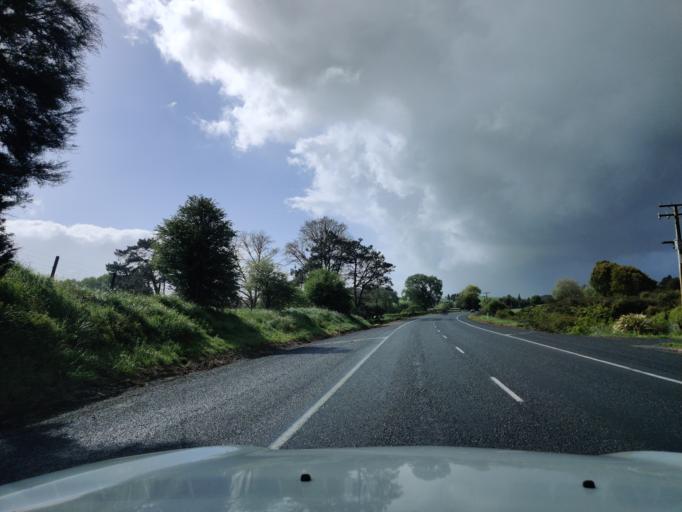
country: NZ
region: Waikato
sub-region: Waipa District
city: Cambridge
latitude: -37.9251
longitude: 175.5662
